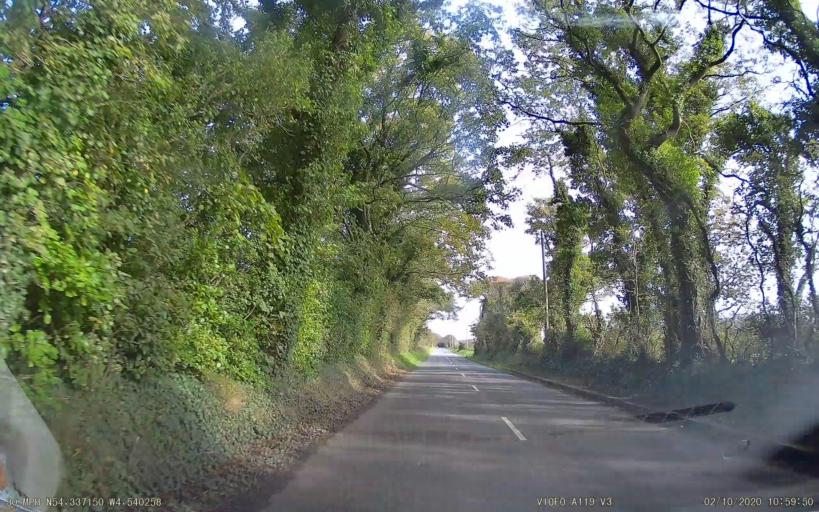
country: IM
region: Ramsey
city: Ramsey
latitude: 54.3371
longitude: -4.5403
